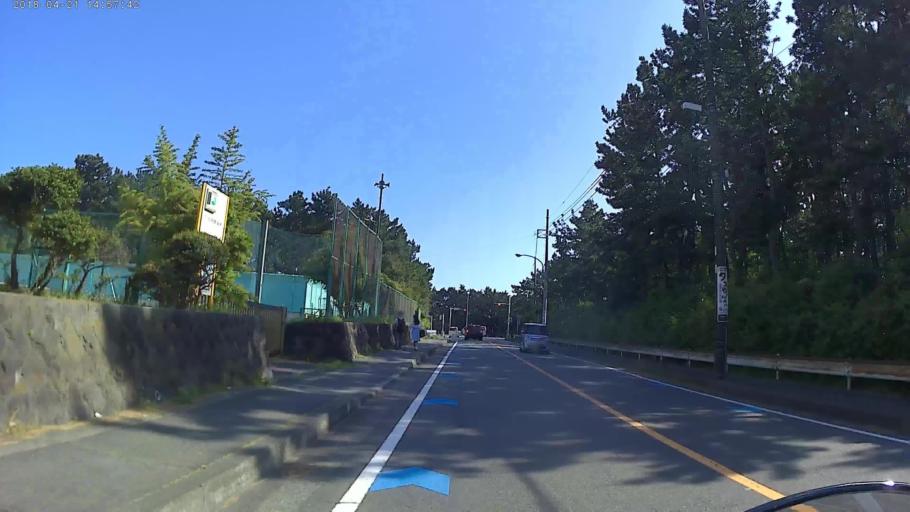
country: JP
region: Kanagawa
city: Chigasaki
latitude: 35.3182
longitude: 139.3869
